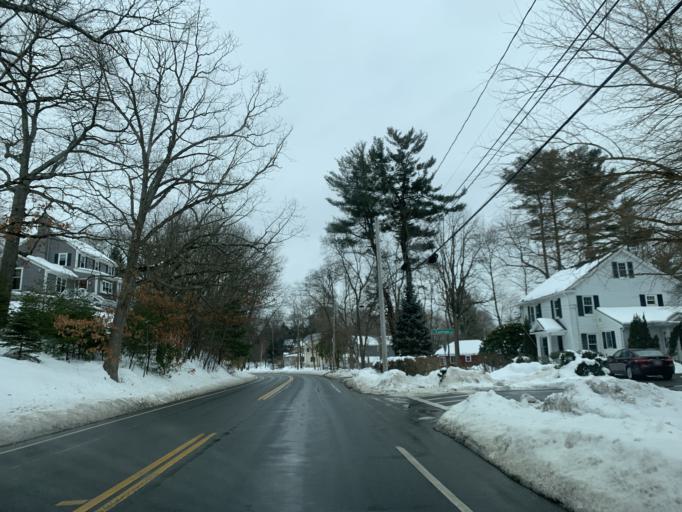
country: US
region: Massachusetts
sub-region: Norfolk County
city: Westwood
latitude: 42.2122
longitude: -71.2258
